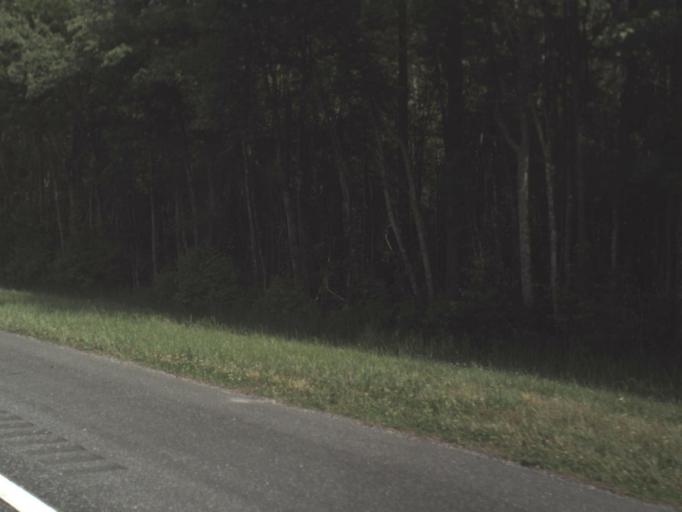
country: US
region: Florida
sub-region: Columbia County
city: Watertown
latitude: 30.2499
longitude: -82.5333
